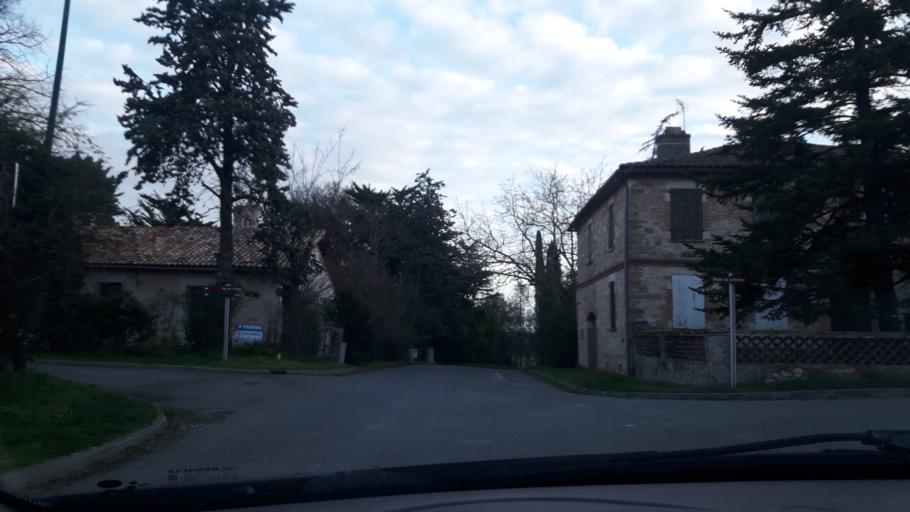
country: FR
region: Midi-Pyrenees
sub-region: Departement du Gers
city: Pujaudran
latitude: 43.6618
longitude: 1.0253
